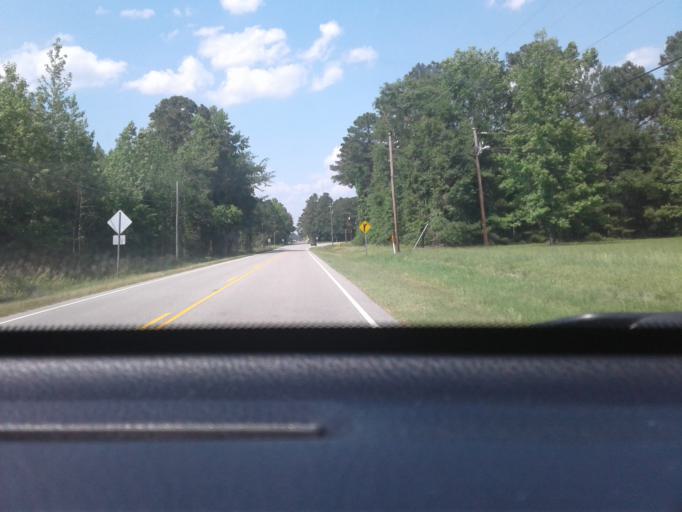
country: US
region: North Carolina
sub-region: Cumberland County
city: Eastover
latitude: 35.1707
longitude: -78.7231
